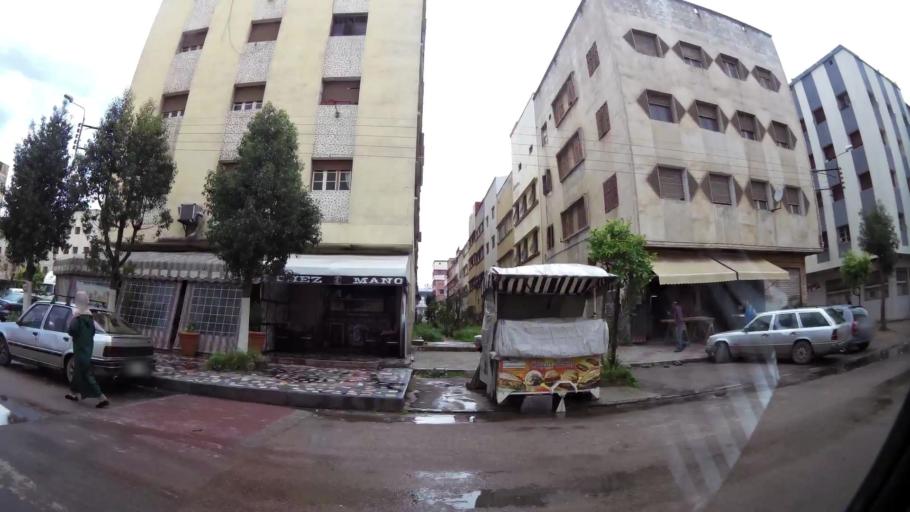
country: MA
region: Grand Casablanca
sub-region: Casablanca
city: Casablanca
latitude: 33.5421
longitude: -7.5689
